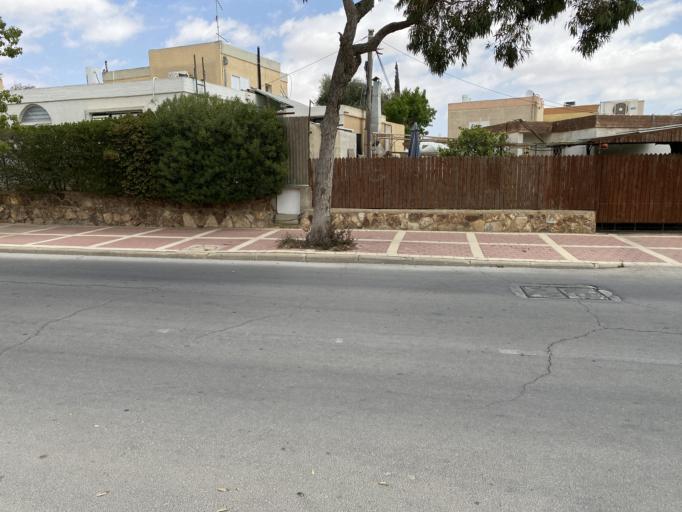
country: IL
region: Southern District
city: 'Arad
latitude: 31.2536
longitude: 35.2148
